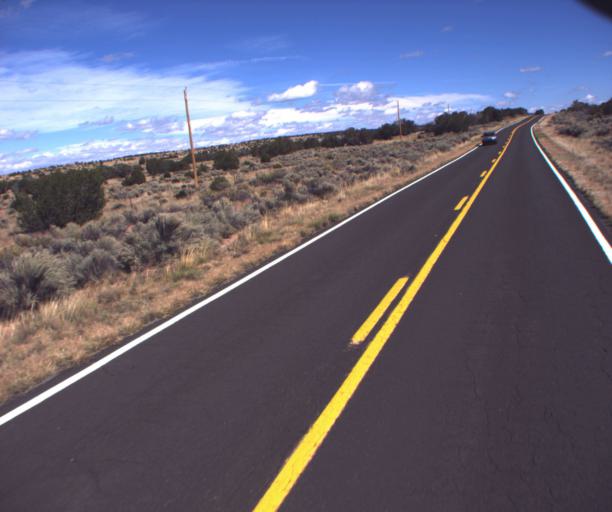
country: US
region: Arizona
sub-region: Apache County
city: Houck
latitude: 34.9190
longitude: -109.2119
